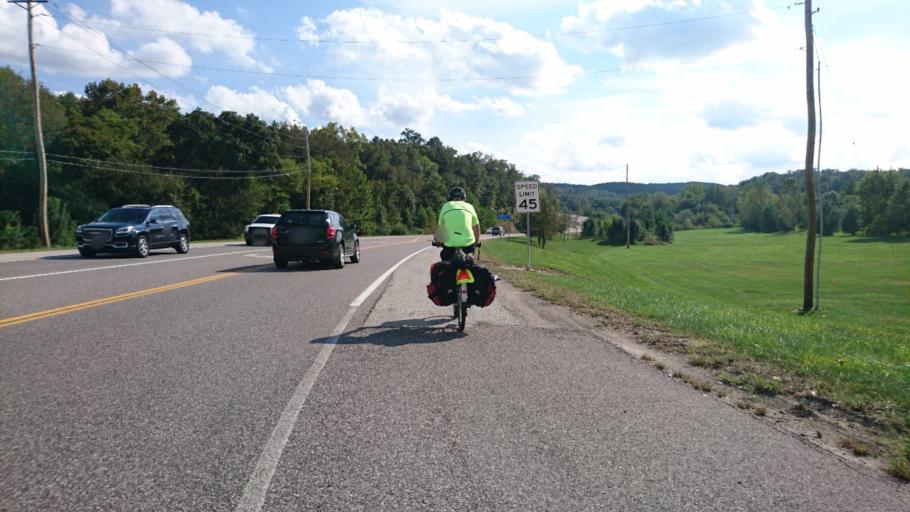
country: US
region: Missouri
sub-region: Saint Louis County
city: Eureka
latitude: 38.5440
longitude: -90.6299
